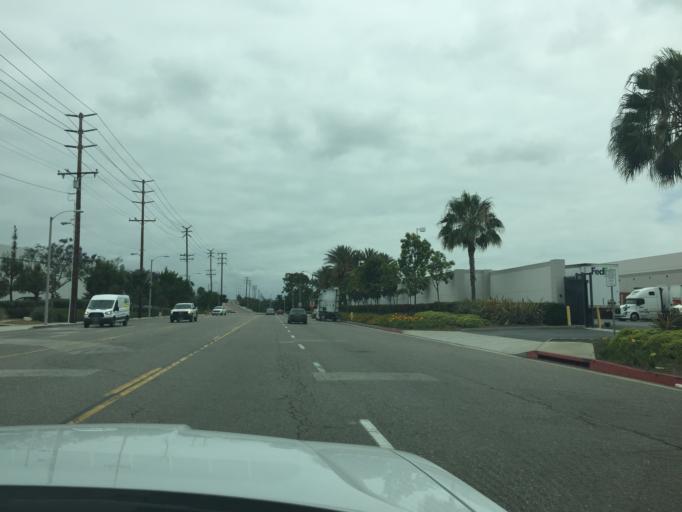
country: US
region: California
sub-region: Los Angeles County
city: Carson
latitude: 33.8317
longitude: -118.2322
